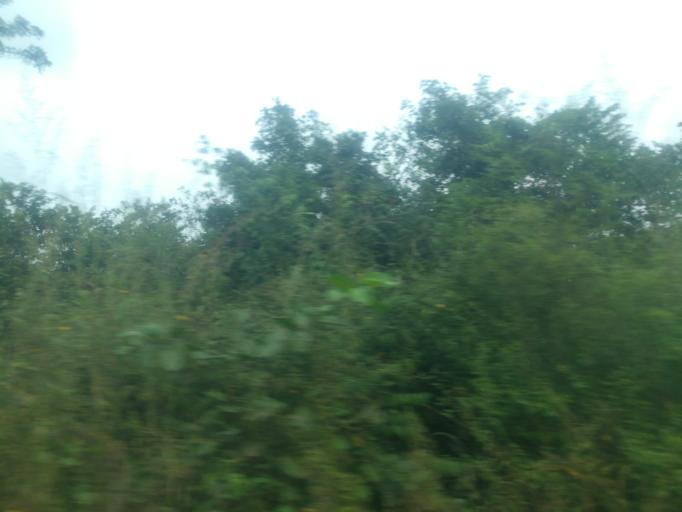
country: NG
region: Ogun
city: Ayetoro
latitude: 7.3484
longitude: 3.0546
